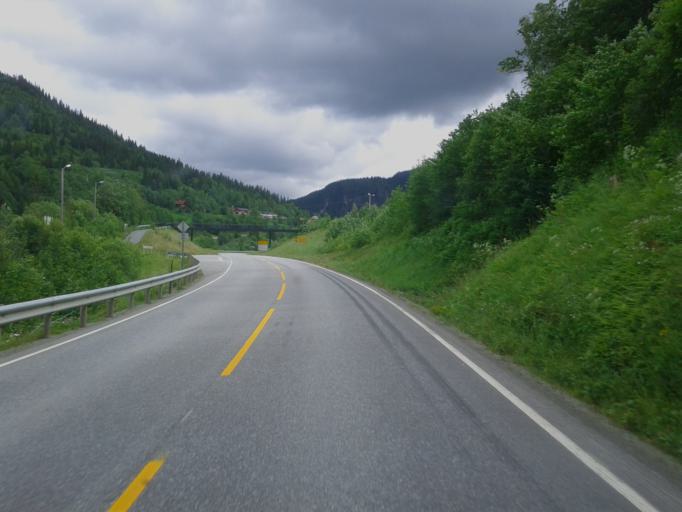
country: NO
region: Sor-Trondelag
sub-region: Midtre Gauldal
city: Storen
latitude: 62.9423
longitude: 10.6471
